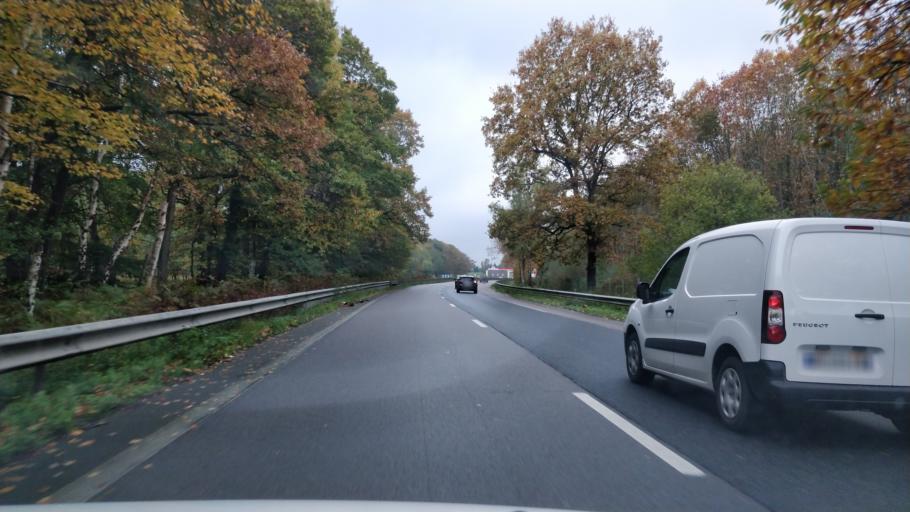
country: FR
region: Haute-Normandie
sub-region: Departement de la Seine-Maritime
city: Grand-Couronne
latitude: 49.3568
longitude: 1.0328
